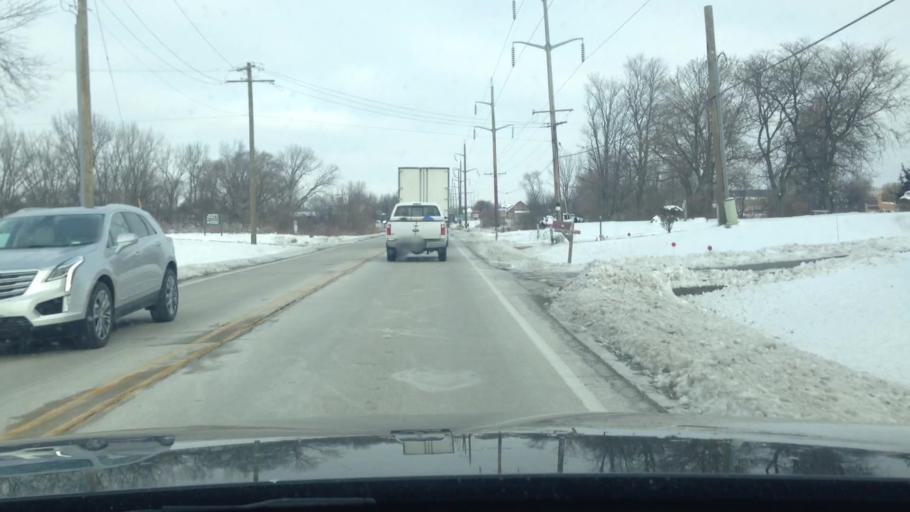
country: US
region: Illinois
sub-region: McHenry County
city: Woodstock
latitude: 42.2848
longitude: -88.4331
